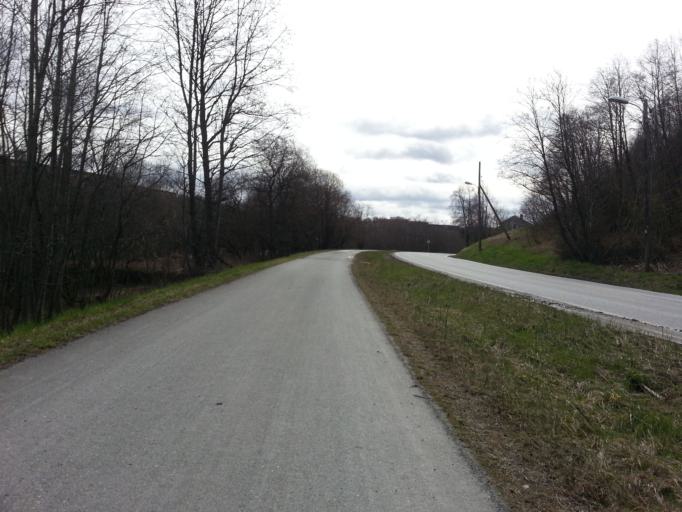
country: NO
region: Sor-Trondelag
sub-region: Trondheim
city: Trondheim
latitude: 63.4033
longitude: 10.3882
